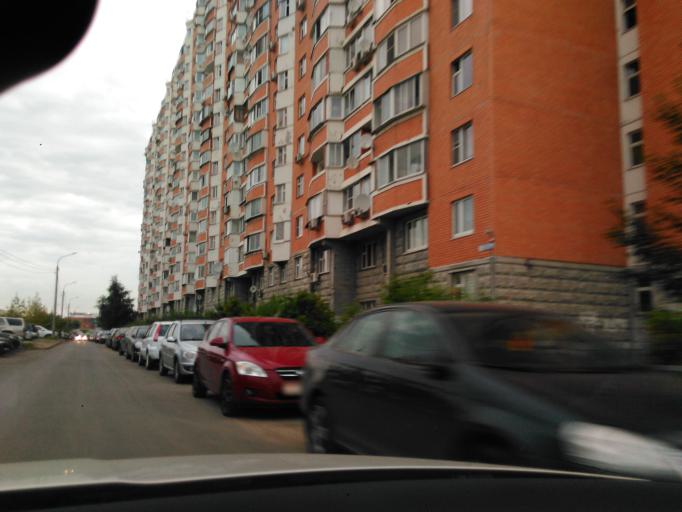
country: RU
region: Moscow
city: Khimki
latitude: 55.9065
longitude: 37.4011
